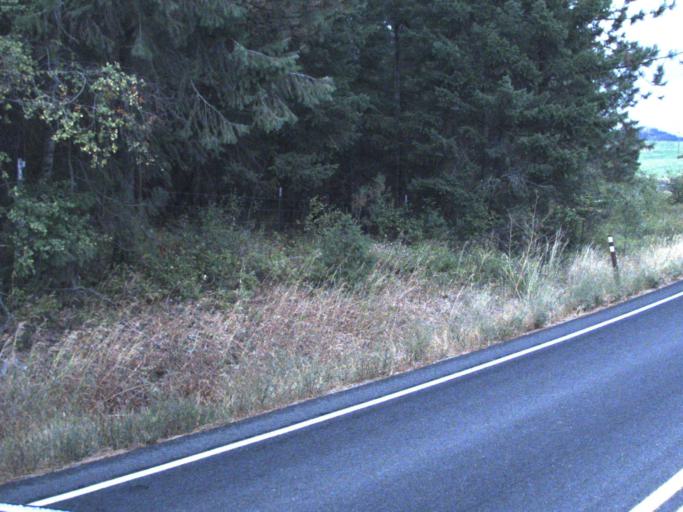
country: US
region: Washington
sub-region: Stevens County
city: Chewelah
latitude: 48.1072
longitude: -117.7557
